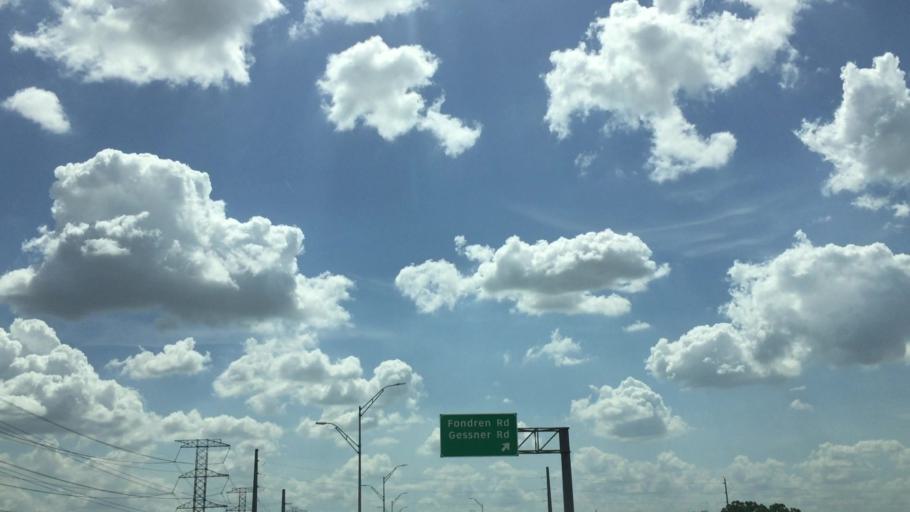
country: US
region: Texas
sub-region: Harris County
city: Piney Point Village
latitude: 29.7221
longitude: -95.5107
